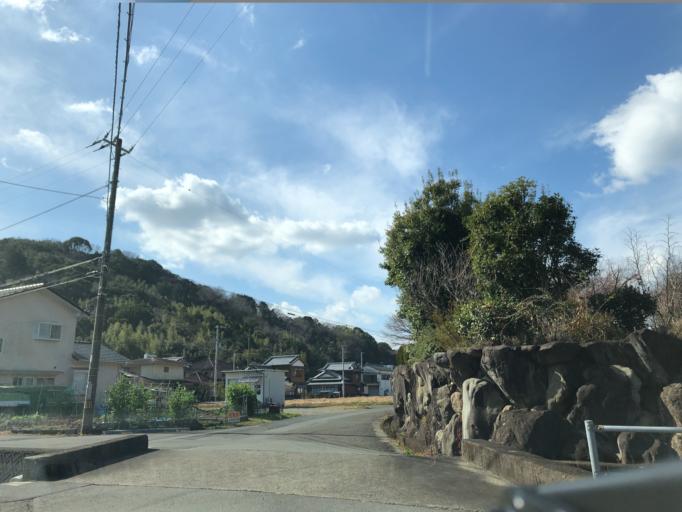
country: JP
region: Kochi
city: Sukumo
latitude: 32.9275
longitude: 132.6863
